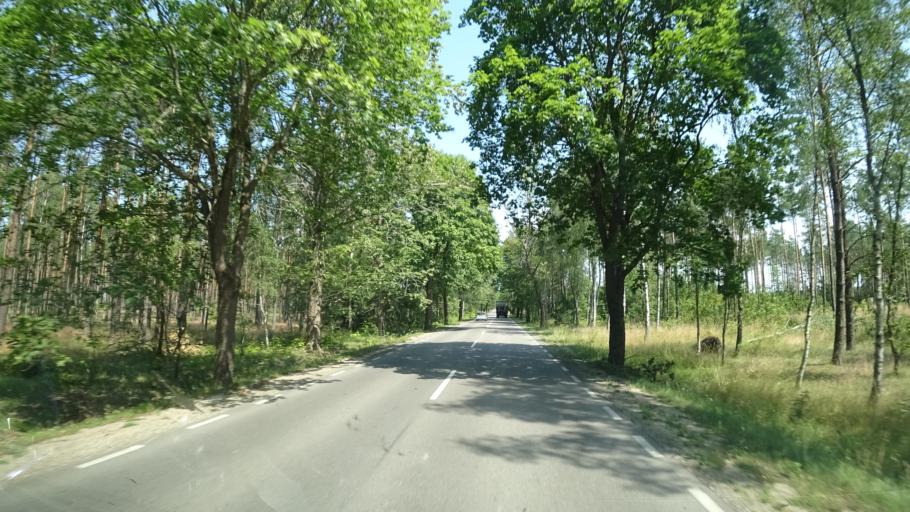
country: PL
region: Pomeranian Voivodeship
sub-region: Powiat koscierski
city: Lipusz
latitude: 54.1232
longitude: 17.8506
